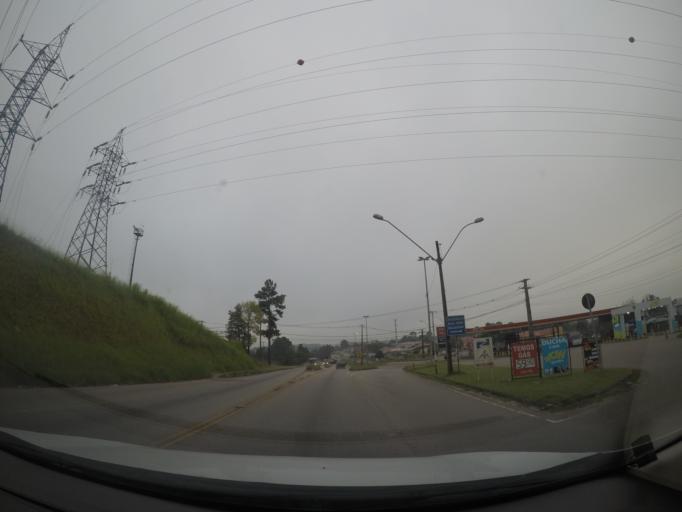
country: BR
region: Parana
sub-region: Curitiba
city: Curitiba
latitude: -25.3726
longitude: -49.2744
